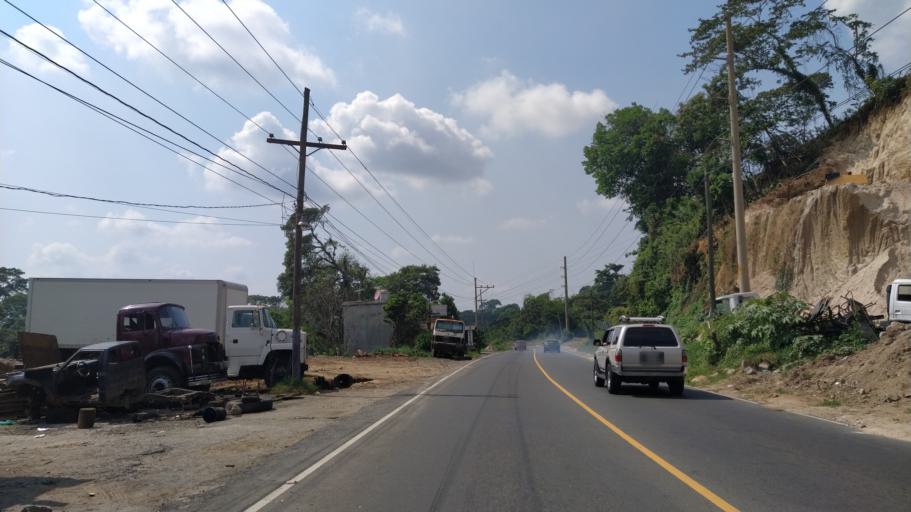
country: GT
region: Quetzaltenango
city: El Palmar
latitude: 14.6424
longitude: -91.5742
